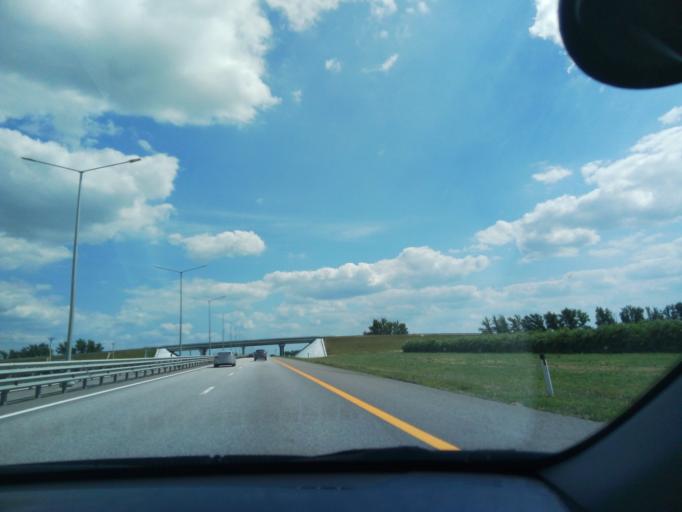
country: RU
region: Voronezj
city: Podkletnoye
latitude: 51.5714
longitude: 39.4716
